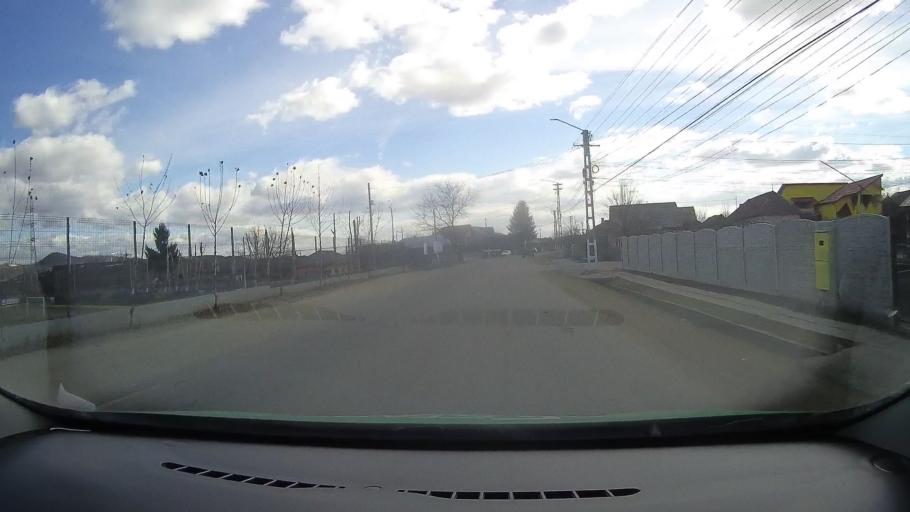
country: RO
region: Dambovita
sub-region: Comuna Doicesti
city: Doicesti
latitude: 44.9850
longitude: 25.3860
